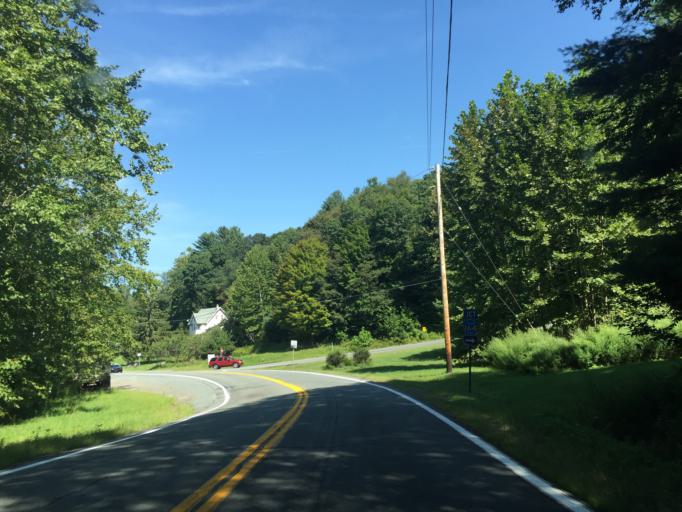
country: US
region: New York
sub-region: Sullivan County
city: Livingston Manor
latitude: 41.7546
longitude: -75.0238
